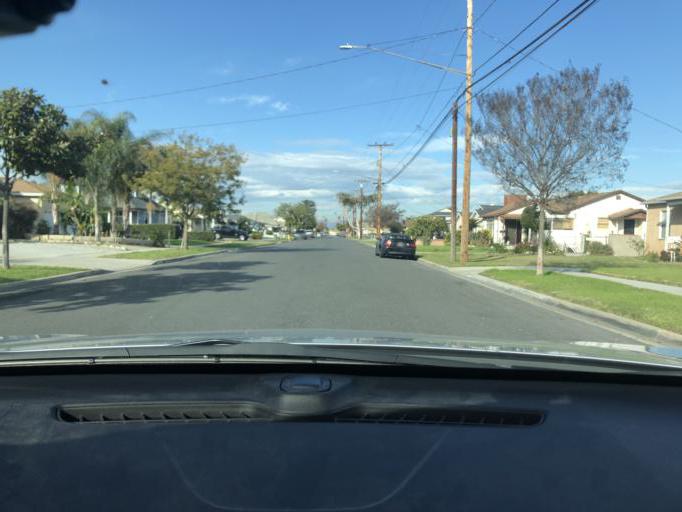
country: US
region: California
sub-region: Los Angeles County
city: Gardena
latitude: 33.8756
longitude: -118.3048
